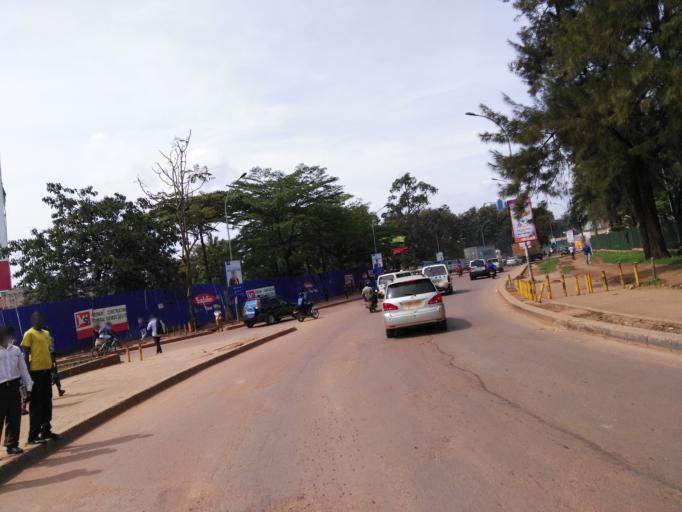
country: UG
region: Central Region
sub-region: Kampala District
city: Kampala
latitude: 0.3063
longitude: 32.5766
